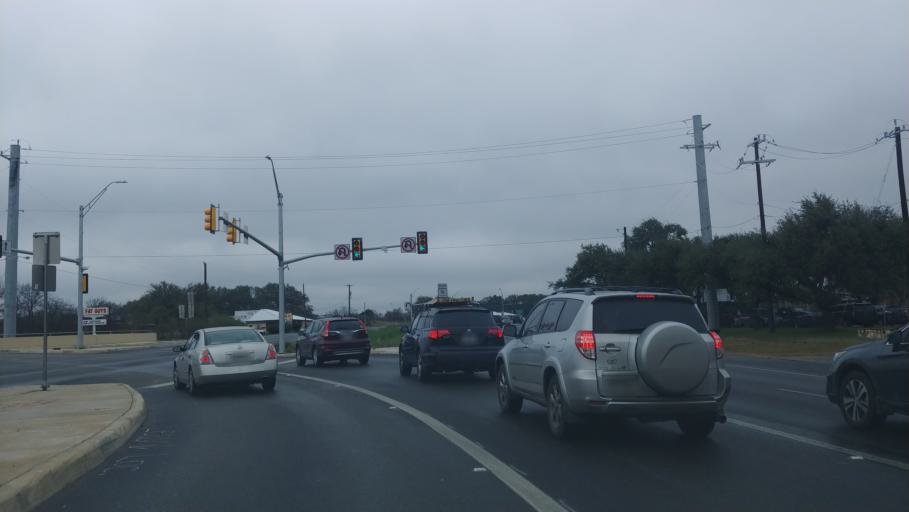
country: US
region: Texas
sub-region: Bexar County
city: Helotes
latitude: 29.5651
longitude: -98.6882
